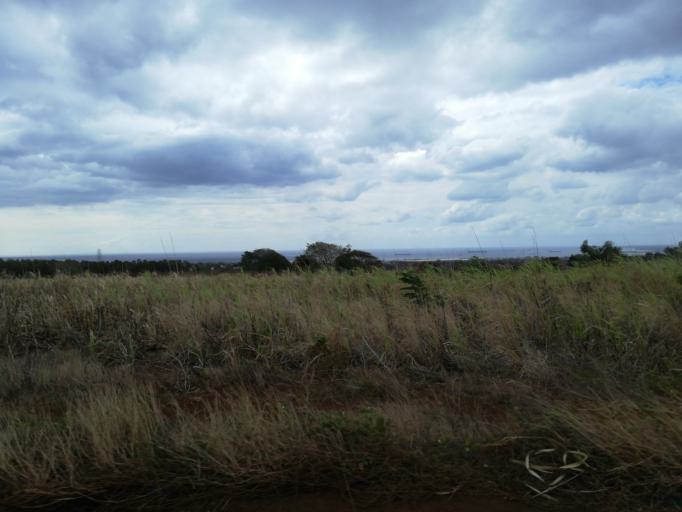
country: MU
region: Black River
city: Petite Riviere
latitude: -20.2079
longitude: 57.4560
